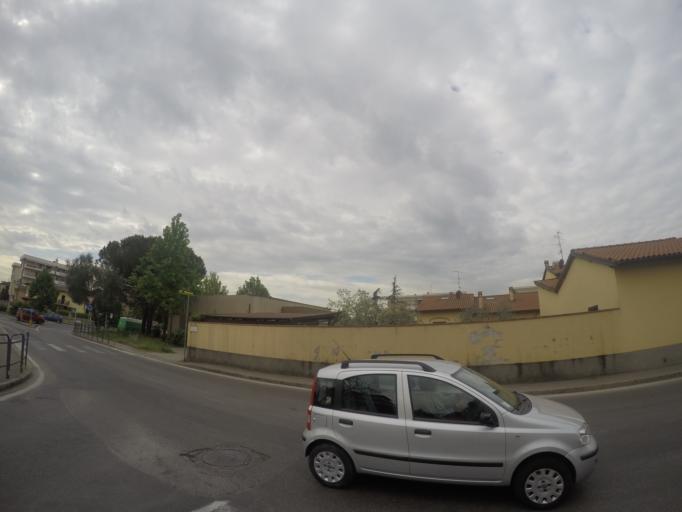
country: IT
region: Tuscany
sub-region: Provincia di Prato
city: Fornacelle
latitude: 43.8901
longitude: 11.0494
